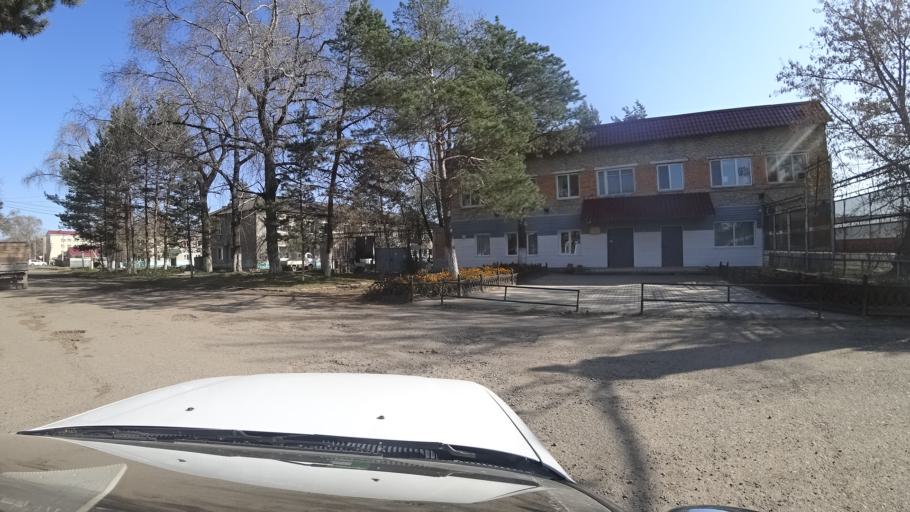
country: RU
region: Primorskiy
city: Dal'nerechensk
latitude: 45.9358
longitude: 133.7165
